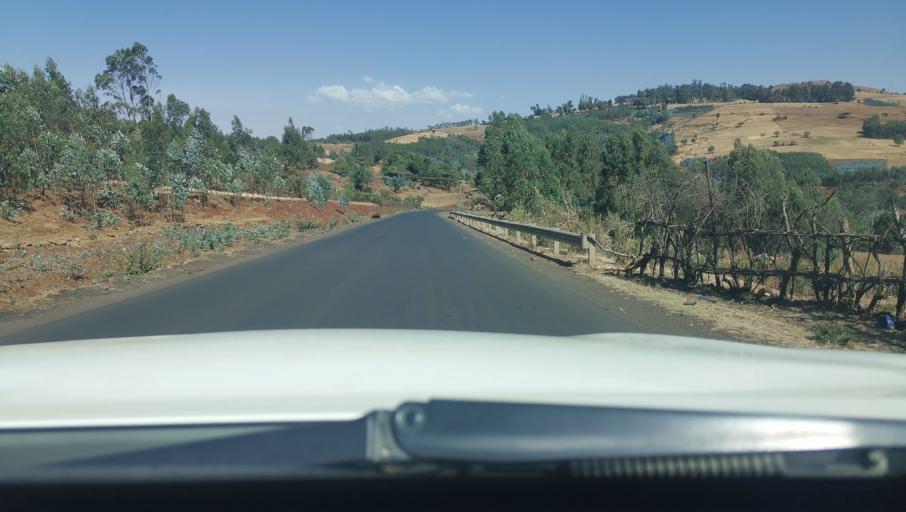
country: ET
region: Oromiya
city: Gedo
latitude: 8.9811
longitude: 37.4660
